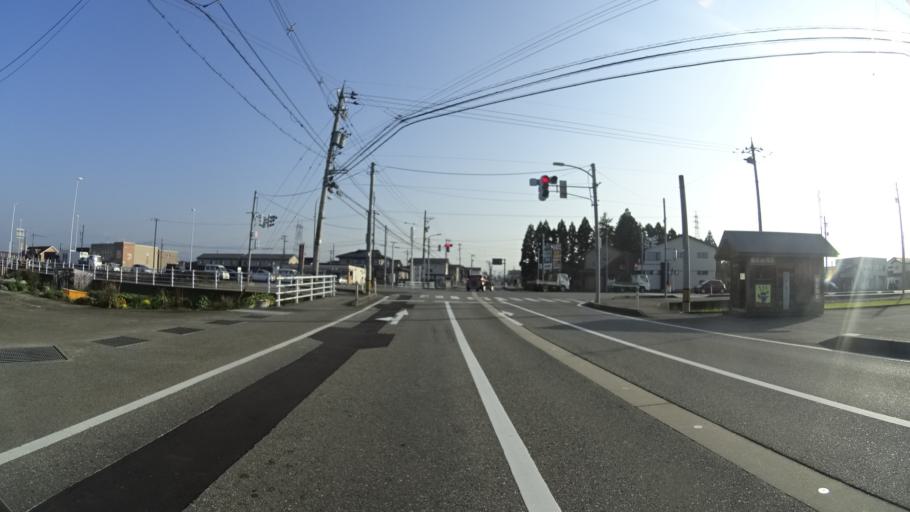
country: JP
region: Toyama
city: Toyama-shi
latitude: 36.6850
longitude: 137.2718
